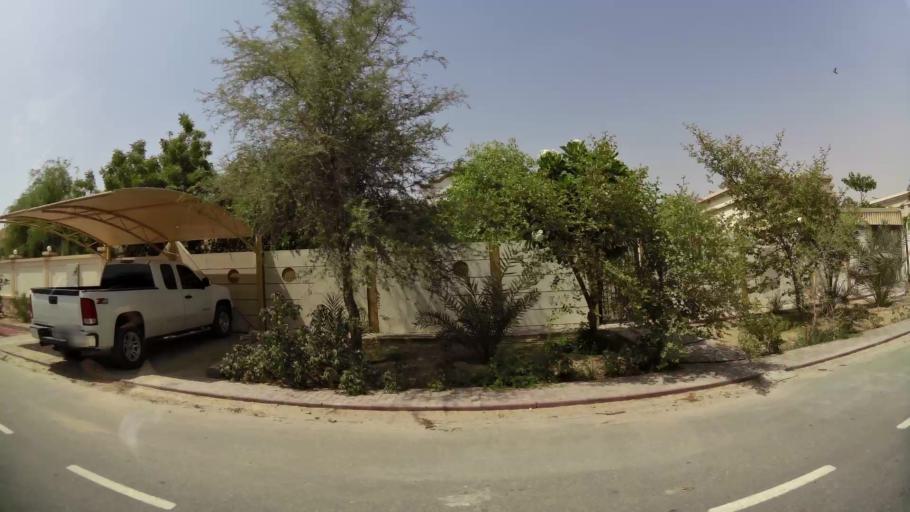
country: AE
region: Ash Shariqah
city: Sharjah
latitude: 25.2397
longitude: 55.4296
